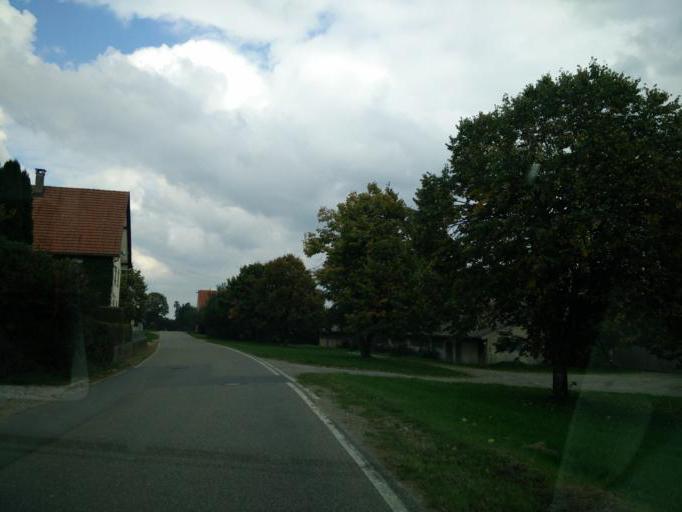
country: DE
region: Baden-Wuerttemberg
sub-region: Tuebingen Region
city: Bad Wurzach
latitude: 47.9402
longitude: 9.9026
